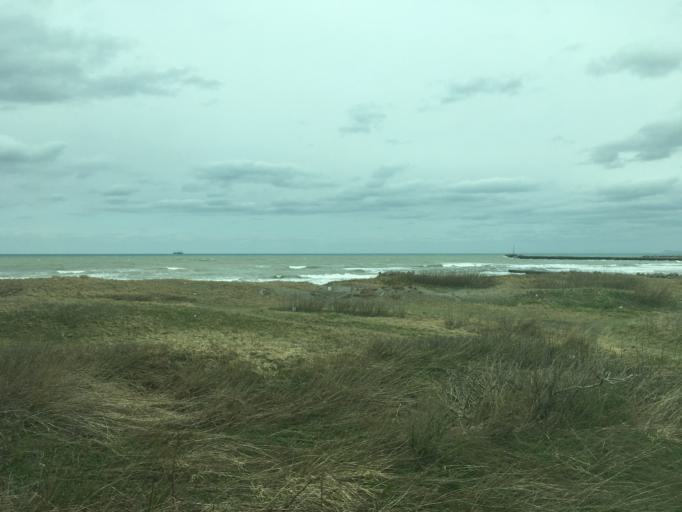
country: JP
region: Aomori
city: Shimokizukuri
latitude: 40.7869
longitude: 140.2381
